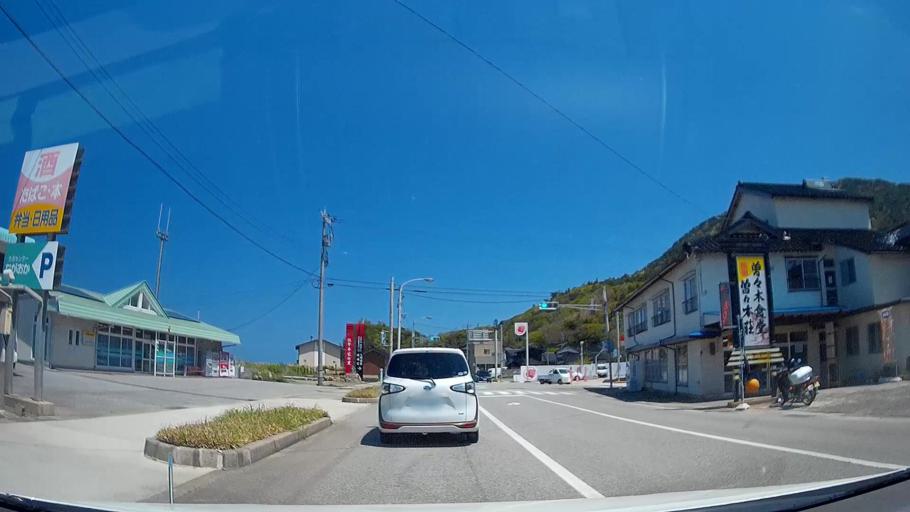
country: JP
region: Ishikawa
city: Nanao
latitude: 37.4527
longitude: 137.0727
